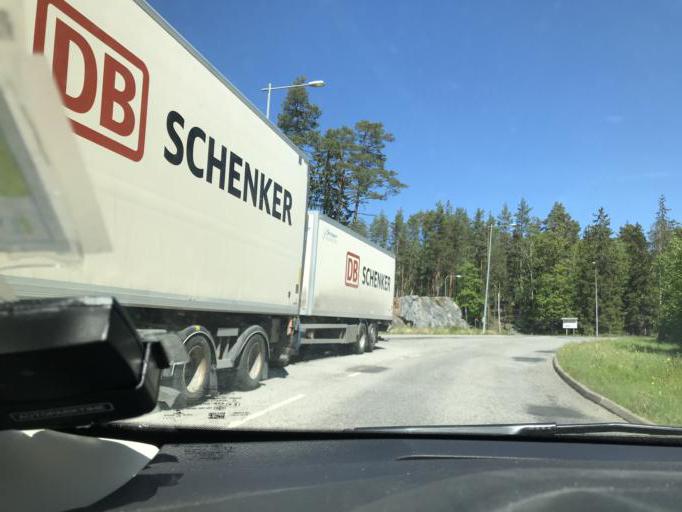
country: SE
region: Stockholm
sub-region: Botkyrka Kommun
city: Tumba
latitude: 59.2127
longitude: 17.8434
